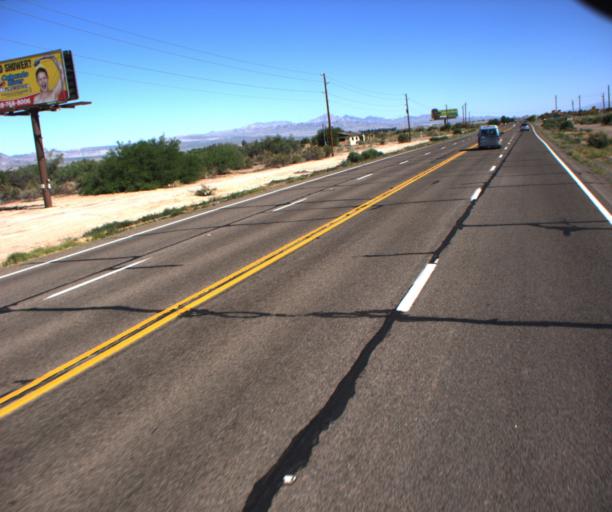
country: US
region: Arizona
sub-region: Mohave County
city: Mohave Valley
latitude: 34.9502
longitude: -114.5979
